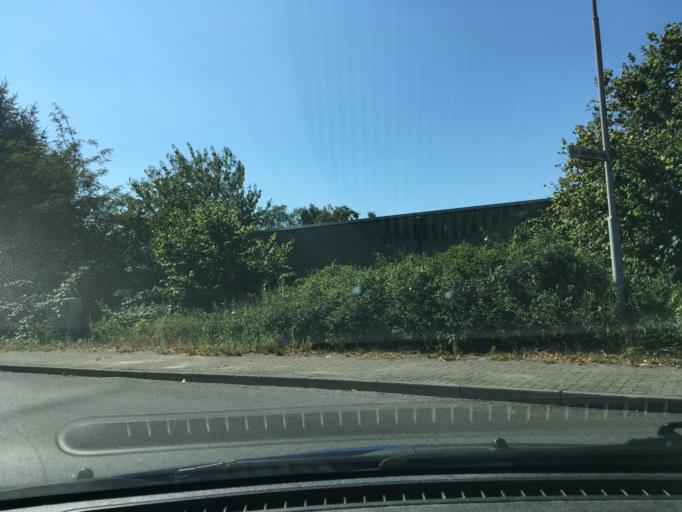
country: DE
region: Hamburg
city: Harburg
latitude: 53.4263
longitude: 10.0412
